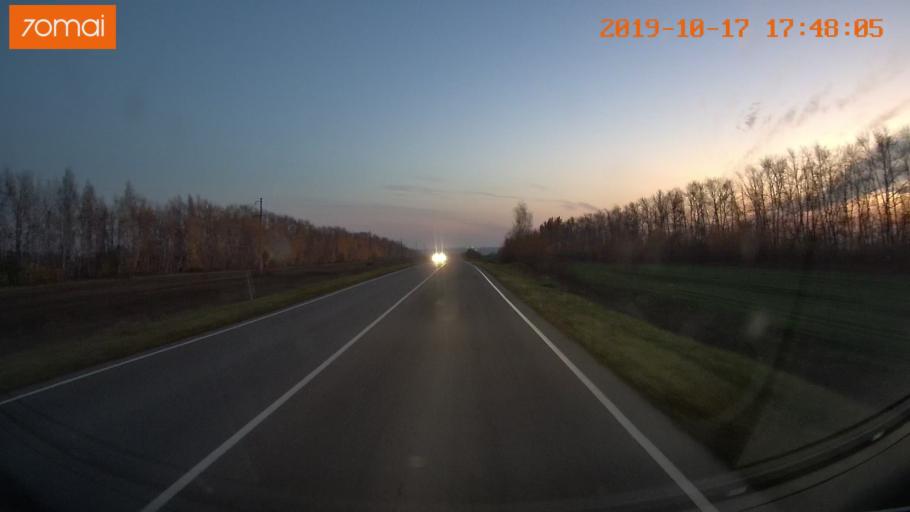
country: RU
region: Tula
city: Yepifan'
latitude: 53.6977
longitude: 38.6966
